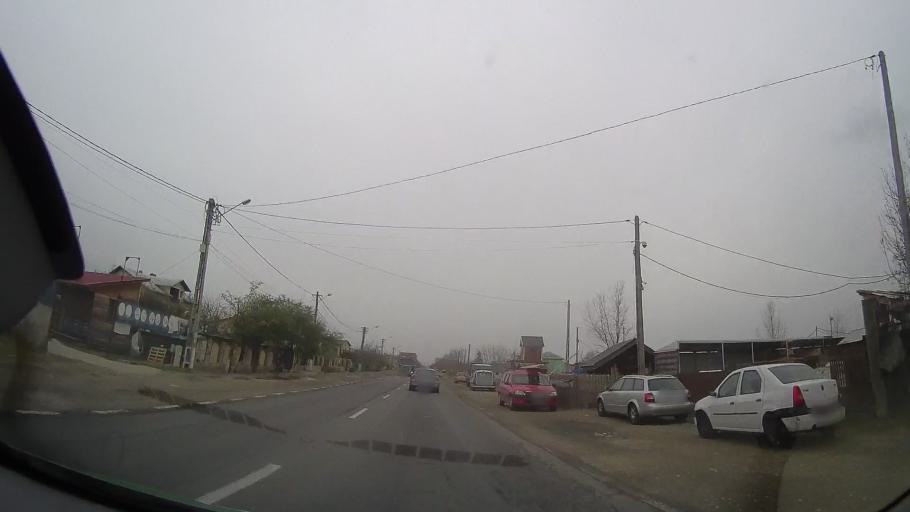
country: RO
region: Prahova
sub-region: Comuna Blejoiu
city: Ploiestiori
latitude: 44.9727
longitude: 26.0209
